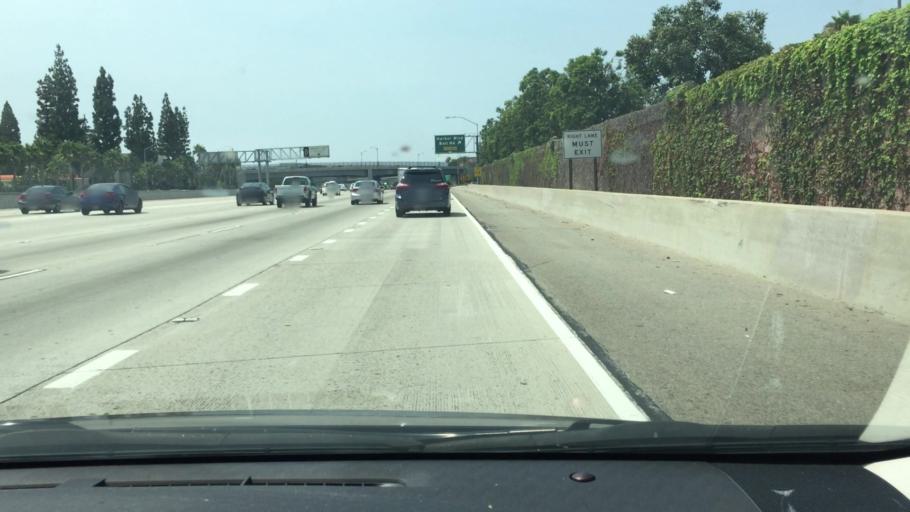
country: US
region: California
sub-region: Orange County
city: Anaheim
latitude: 33.8130
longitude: -117.9120
